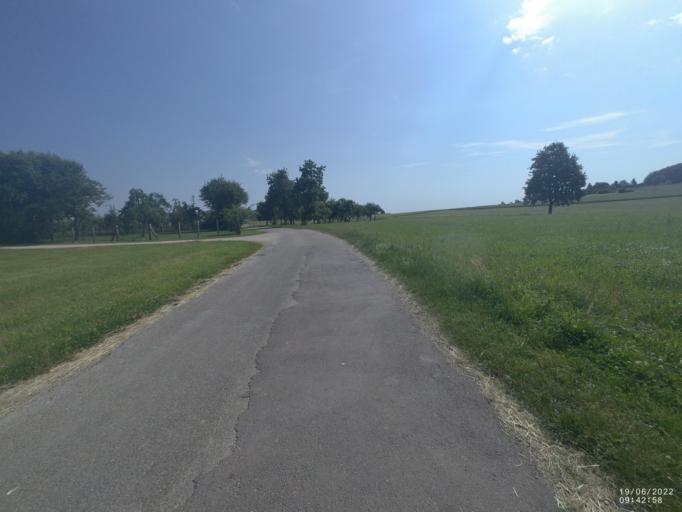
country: DE
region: Baden-Wuerttemberg
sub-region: Regierungsbezirk Stuttgart
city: Gerstetten
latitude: 48.6144
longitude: 10.0230
